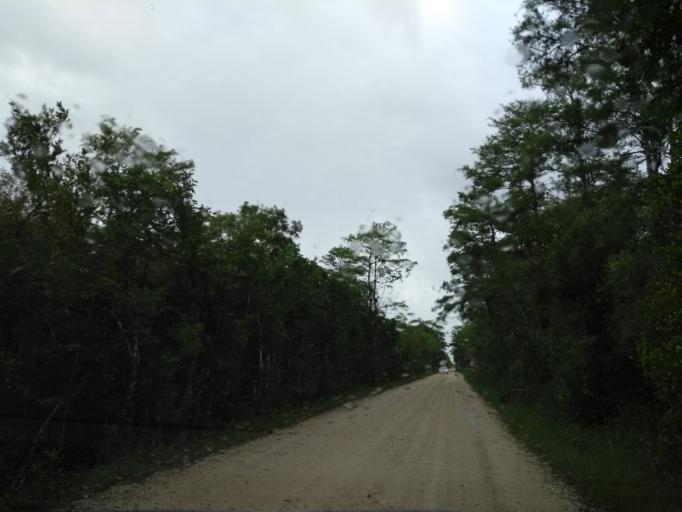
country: US
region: Florida
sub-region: Miami-Dade County
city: The Hammocks
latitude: 25.7604
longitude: -81.0069
